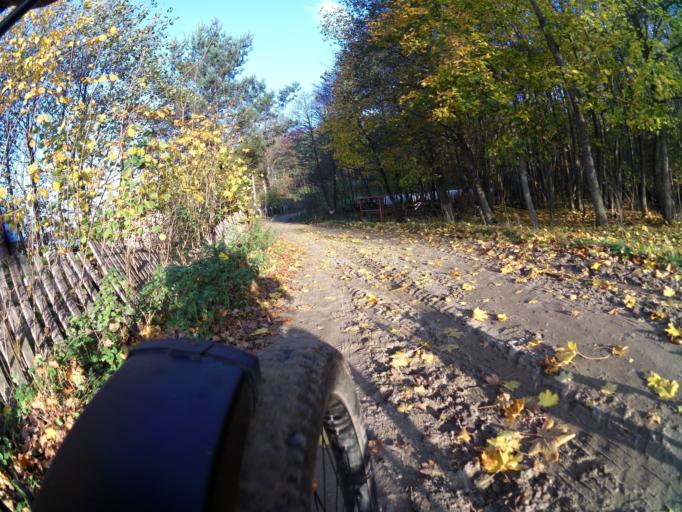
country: PL
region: Pomeranian Voivodeship
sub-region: Powiat pucki
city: Krokowa
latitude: 54.7461
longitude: 18.1949
